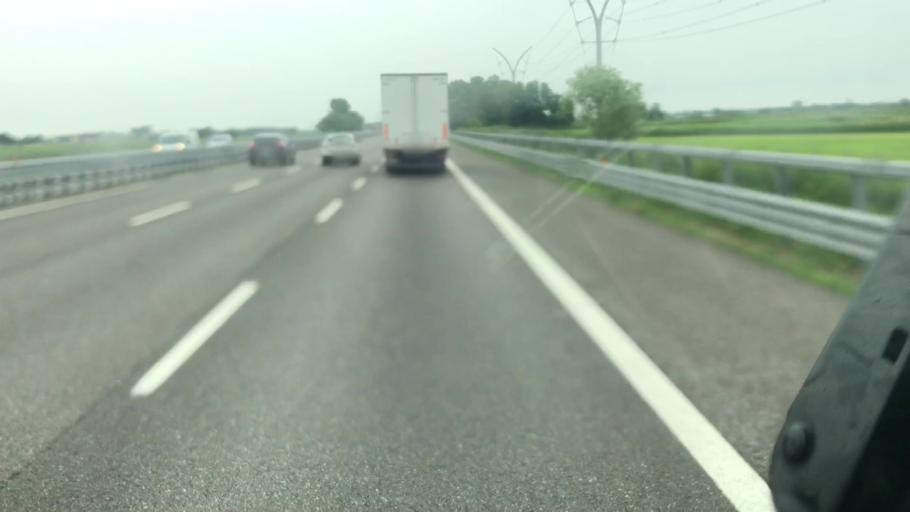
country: IT
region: Lombardy
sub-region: Provincia di Pavia
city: Trivolzio
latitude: 45.2682
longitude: 9.0553
